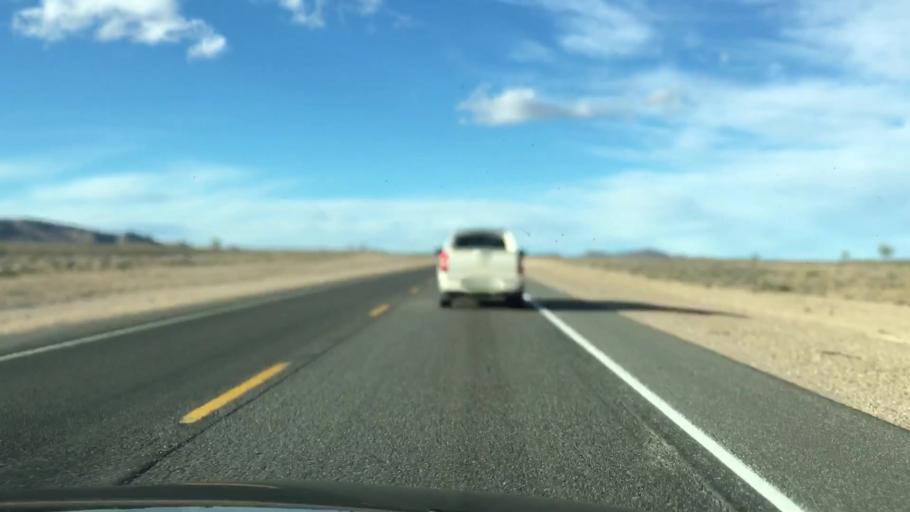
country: US
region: Nevada
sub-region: Esmeralda County
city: Goldfield
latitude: 37.5754
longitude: -117.2031
